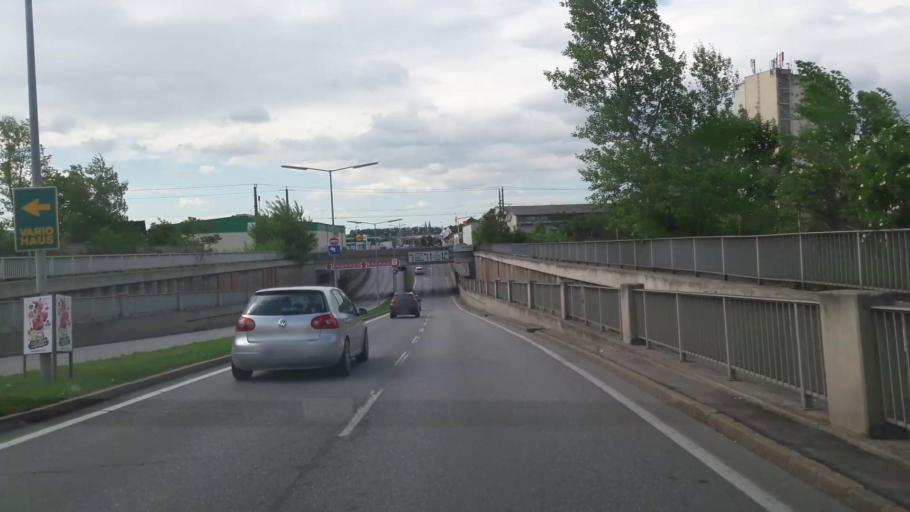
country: AT
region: Lower Austria
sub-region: Politischer Bezirk Wiener Neustadt
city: Theresienfeld
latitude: 47.8320
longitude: 16.2444
